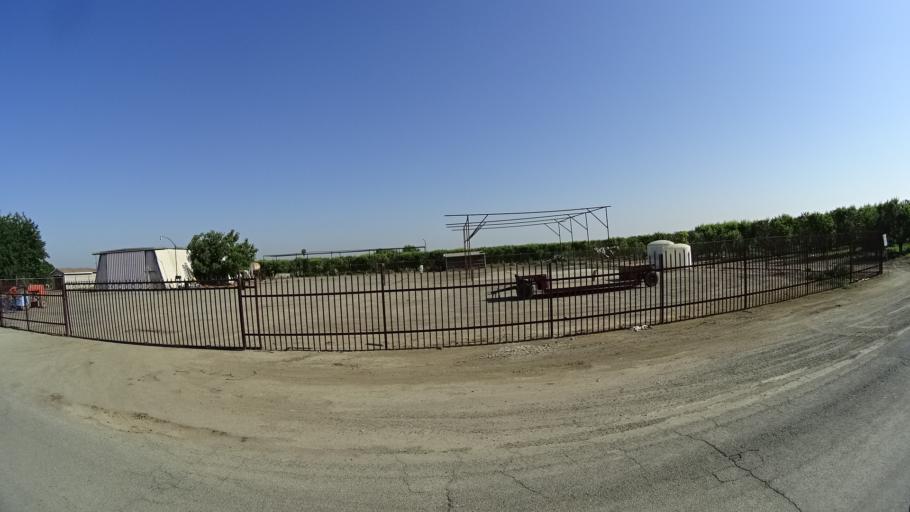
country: US
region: California
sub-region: Kings County
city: Lucerne
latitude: 36.3866
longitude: -119.5807
